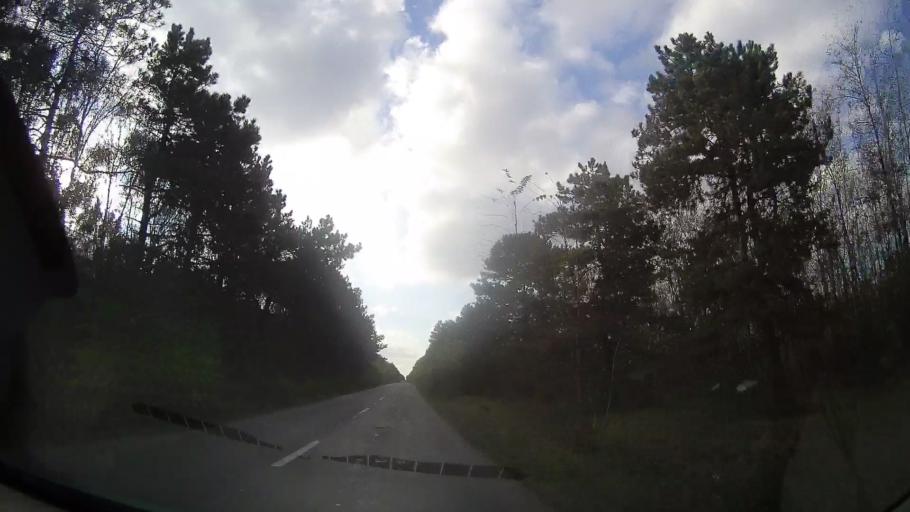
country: RO
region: Constanta
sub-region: Comuna Negru Voda
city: Negru Voda
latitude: 43.8193
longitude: 28.2623
